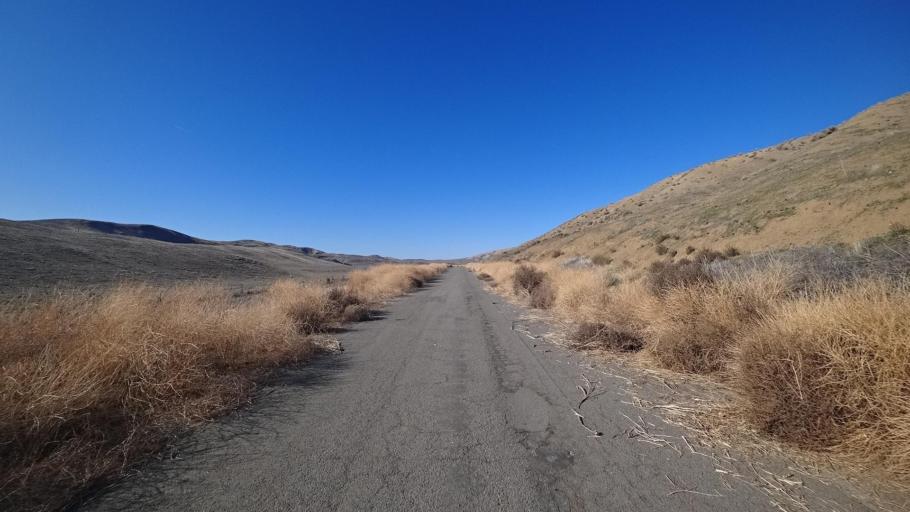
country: US
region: California
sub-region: Kern County
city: Maricopa
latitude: 34.9825
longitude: -119.4701
